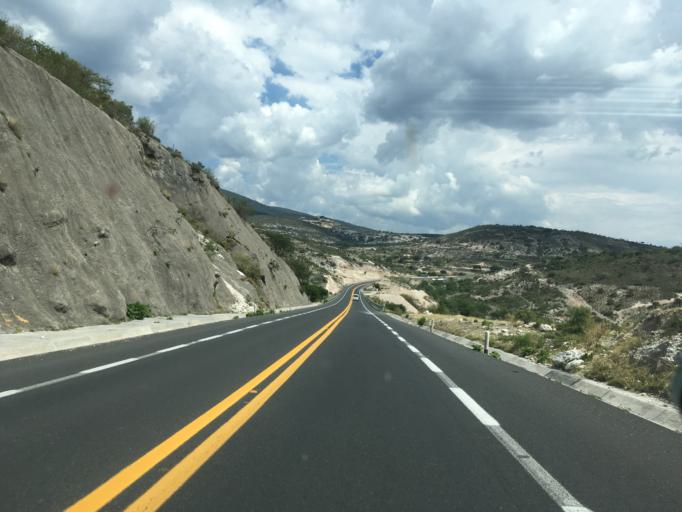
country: MX
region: Oaxaca
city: San Gabriel Casa Blanca
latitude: 17.9895
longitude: -97.3546
